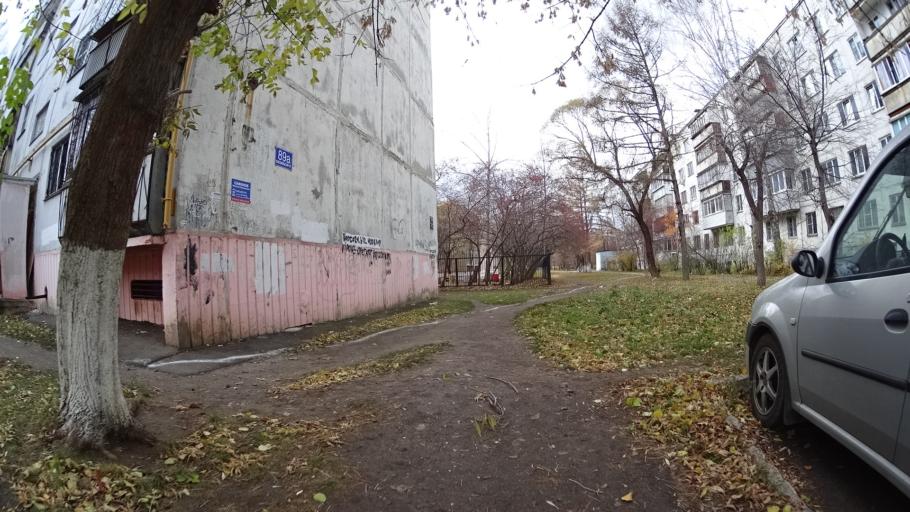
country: RU
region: Chelyabinsk
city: Roshchino
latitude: 55.1932
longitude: 61.3085
